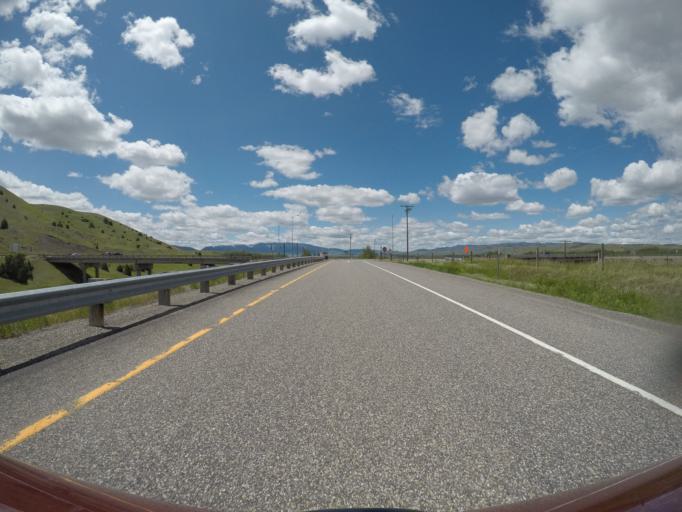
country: US
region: Montana
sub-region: Park County
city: Livingston
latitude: 45.7074
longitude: -110.4546
